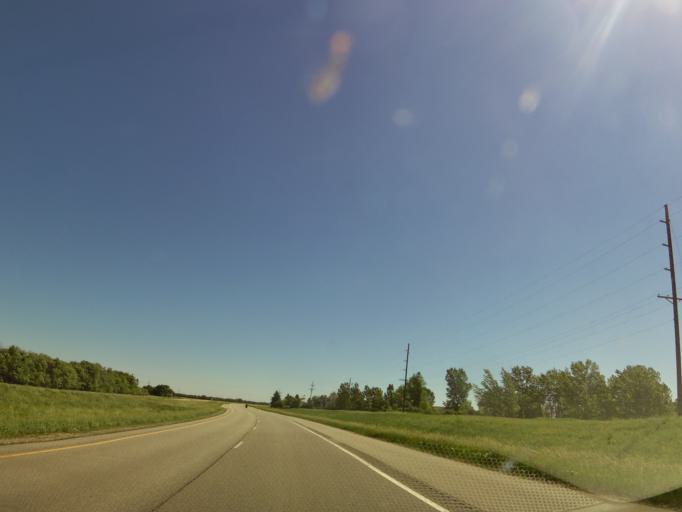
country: US
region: Minnesota
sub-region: Polk County
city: Crookston
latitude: 47.7572
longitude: -96.5498
